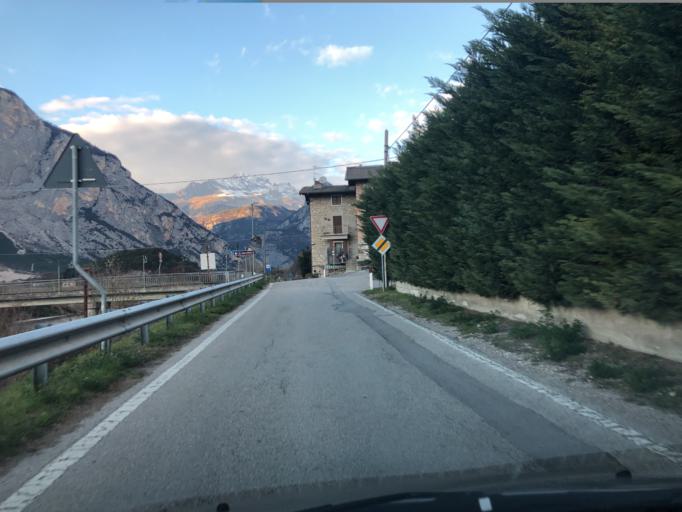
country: IT
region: Trentino-Alto Adige
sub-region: Provincia di Trento
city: Pietramurata
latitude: 46.0164
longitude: 10.9592
